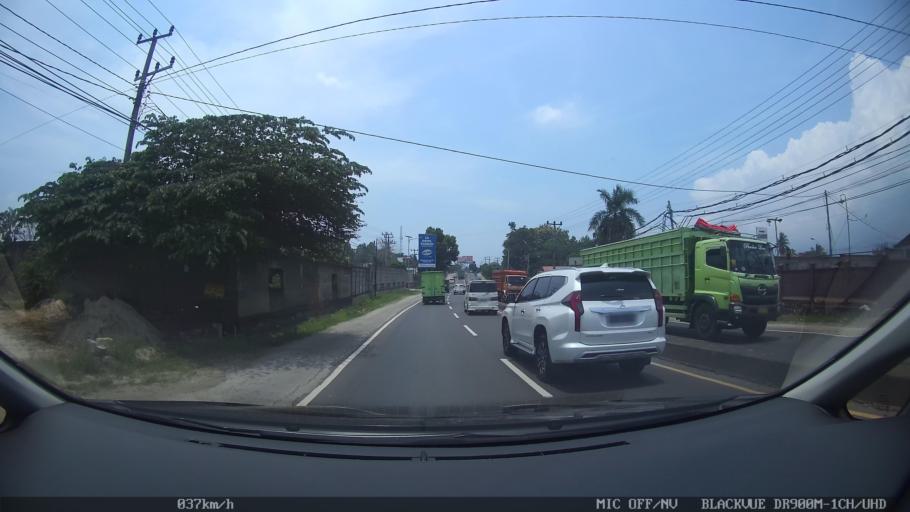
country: ID
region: Lampung
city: Natar
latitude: -5.3404
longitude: 105.2133
